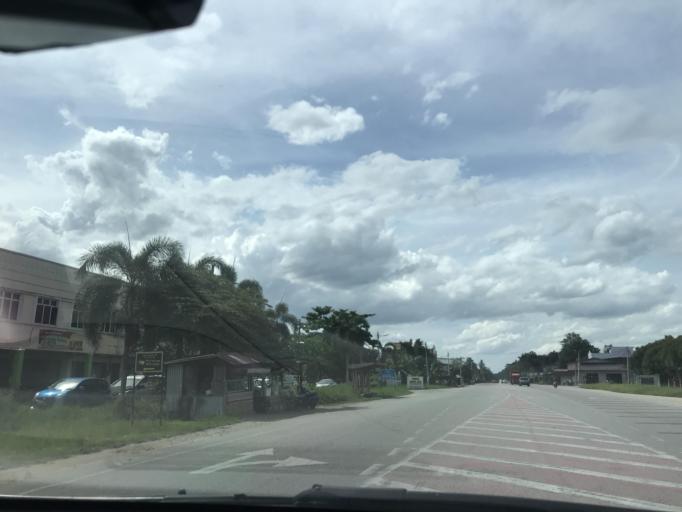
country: MY
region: Kelantan
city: Tanah Merah
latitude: 5.8571
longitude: 102.1680
